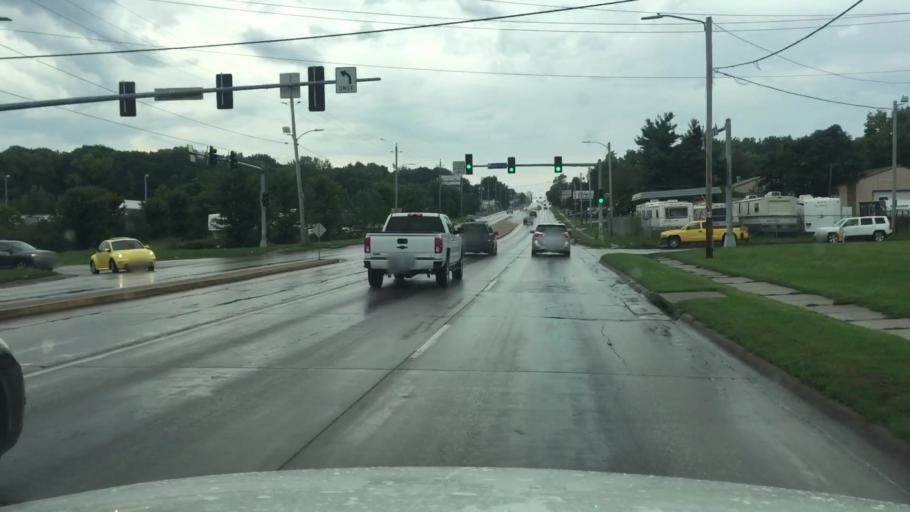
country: US
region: Iowa
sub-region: Polk County
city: Des Moines
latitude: 41.5702
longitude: -93.5971
